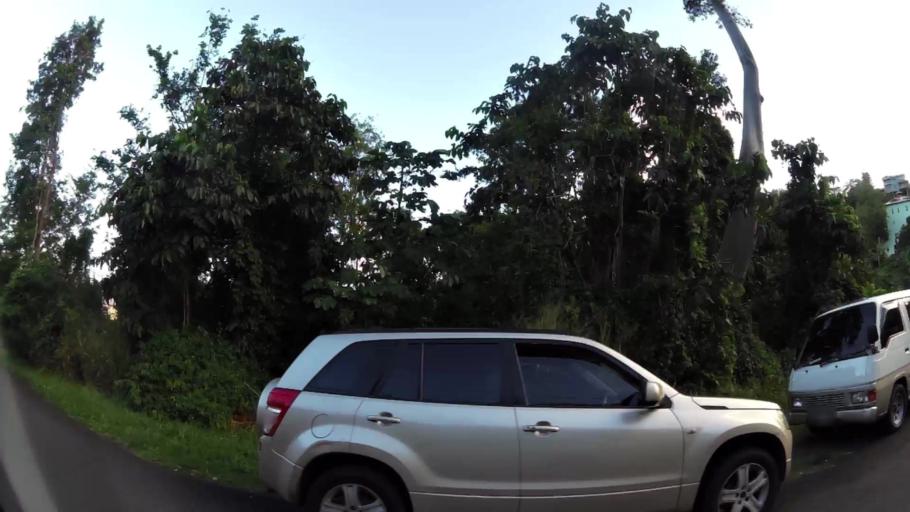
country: LC
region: Castries Quarter
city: Bisee
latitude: 14.0274
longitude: -60.9745
